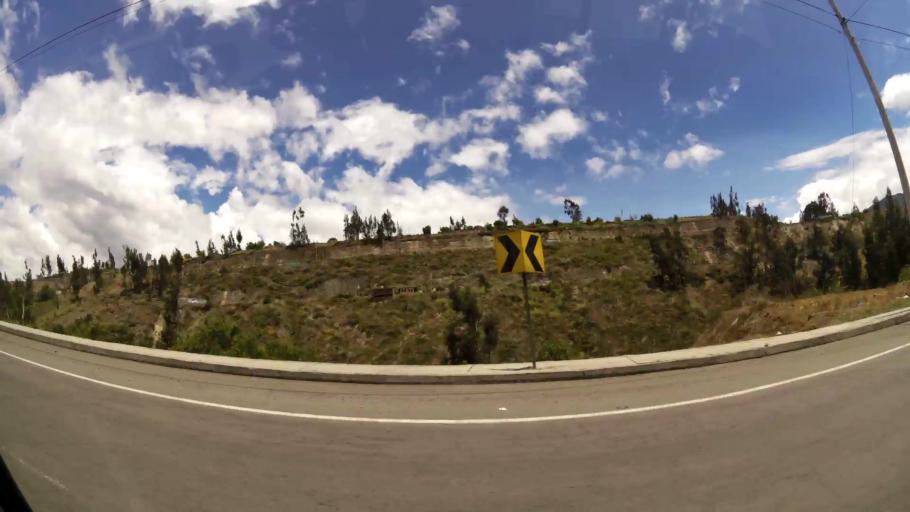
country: EC
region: Tungurahua
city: Pelileo
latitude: -1.3194
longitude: -78.5937
